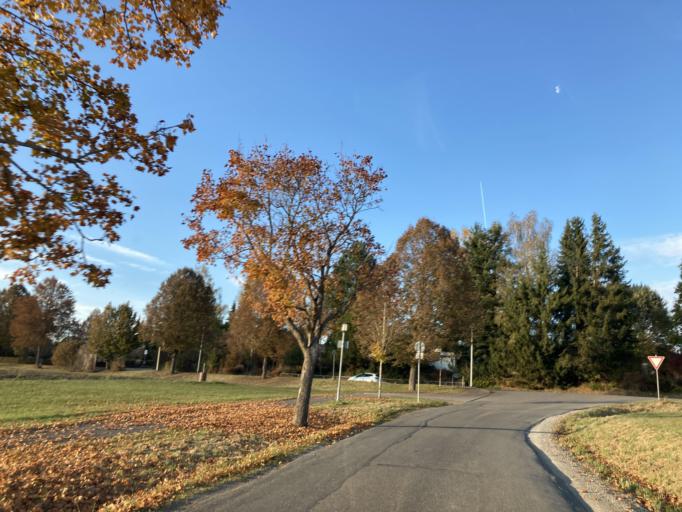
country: DE
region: Baden-Wuerttemberg
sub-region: Freiburg Region
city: Villingen-Schwenningen
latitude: 48.0294
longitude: 8.4505
